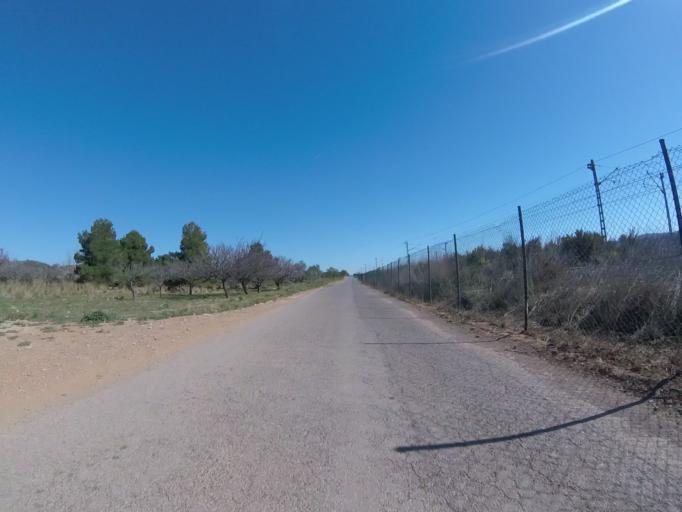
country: ES
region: Valencia
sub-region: Provincia de Castello
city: Alcala de Xivert
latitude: 40.3230
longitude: 0.2380
